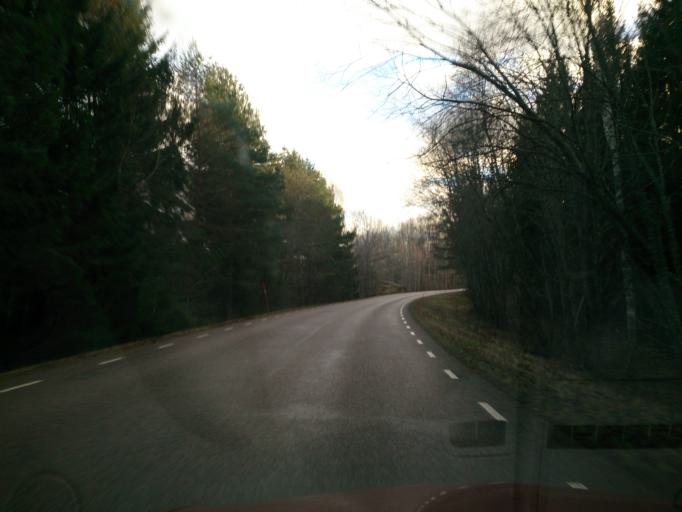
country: SE
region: OEstergoetland
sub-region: Atvidabergs Kommun
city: Atvidaberg
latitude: 58.2356
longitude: 16.0085
